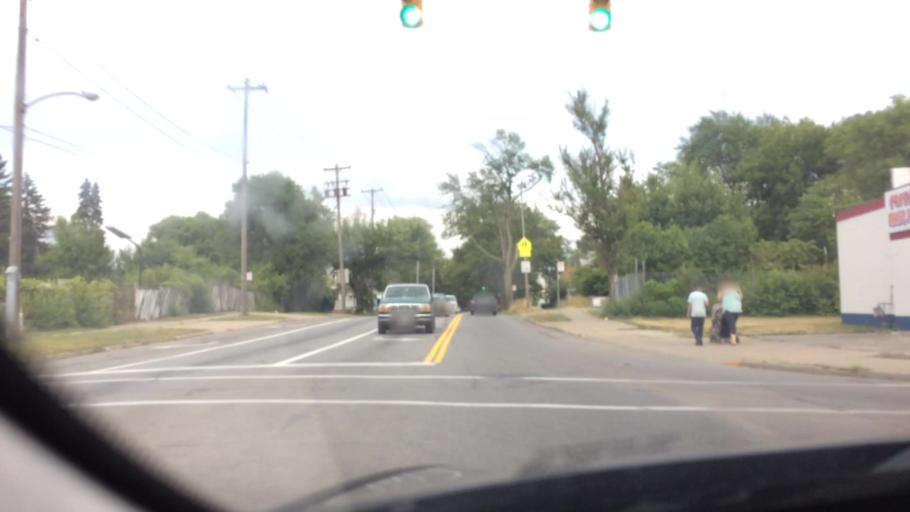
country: US
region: Ohio
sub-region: Wood County
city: Rossford
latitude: 41.6308
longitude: -83.5746
